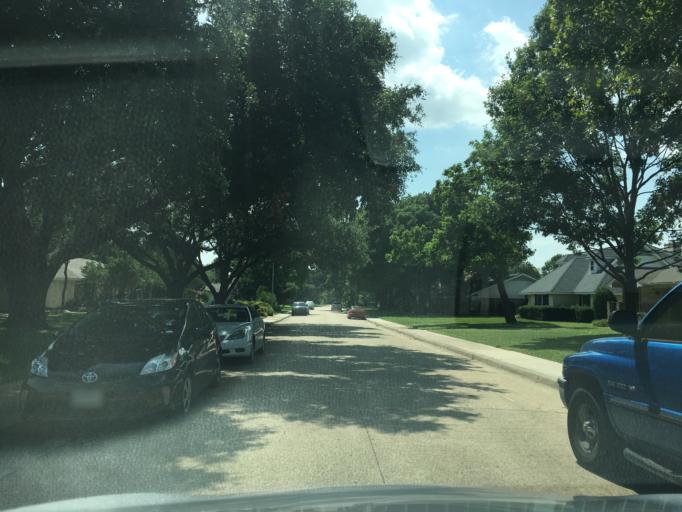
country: US
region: Texas
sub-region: Dallas County
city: Farmers Branch
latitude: 32.9227
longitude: -96.8620
